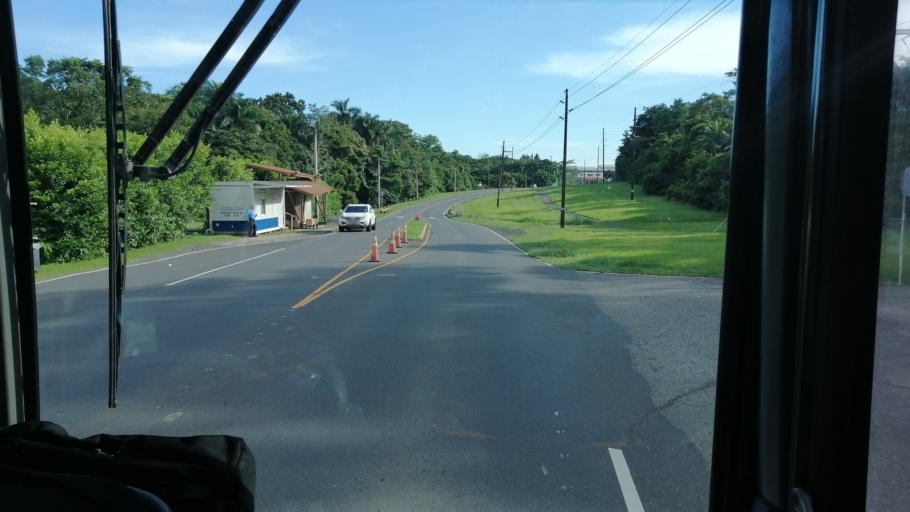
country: PA
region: Panama
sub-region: Distrito de Panama
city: Ancon
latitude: 8.9348
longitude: -79.5910
